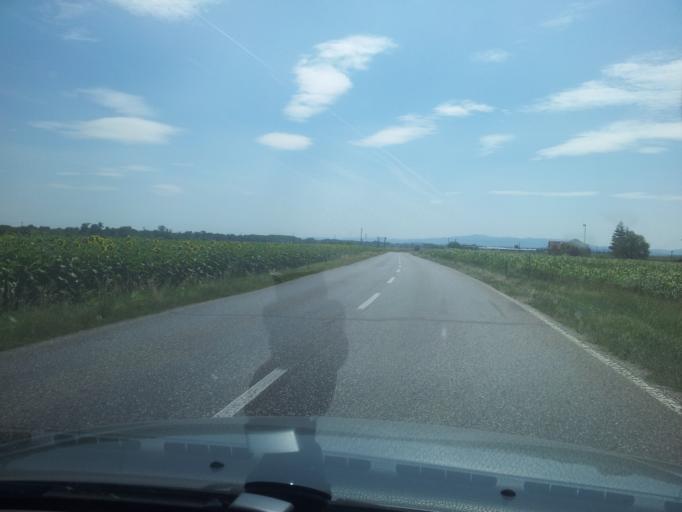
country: SK
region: Nitriansky
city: Zeliezovce
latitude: 48.1217
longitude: 18.6063
